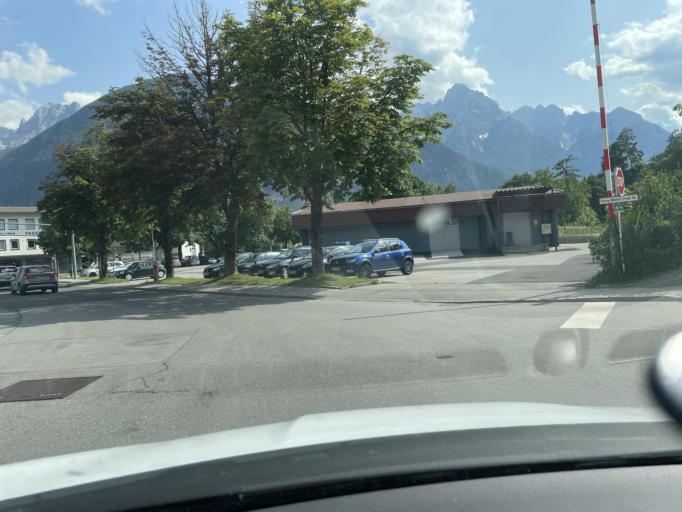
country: AT
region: Tyrol
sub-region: Politischer Bezirk Lienz
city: Lienz
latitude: 46.8314
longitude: 12.7747
